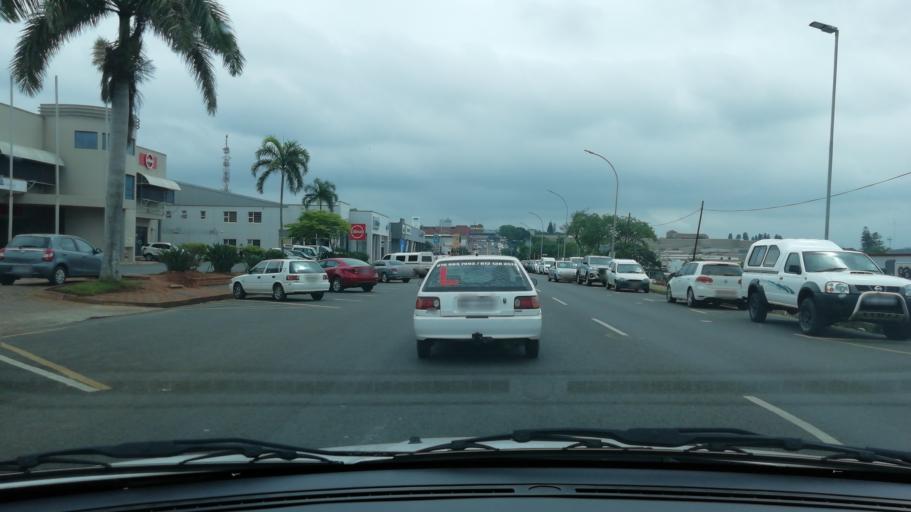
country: ZA
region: KwaZulu-Natal
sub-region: uThungulu District Municipality
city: Empangeni
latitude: -28.7396
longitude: 31.8937
